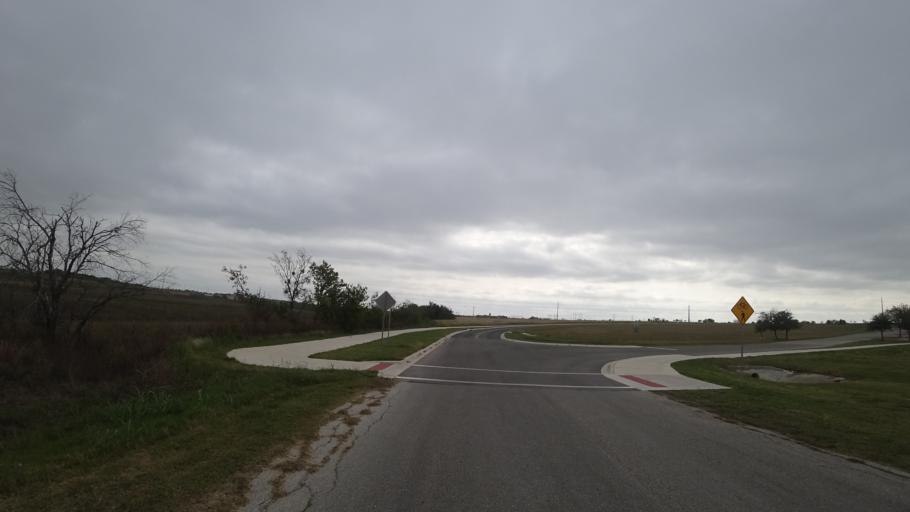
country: US
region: Texas
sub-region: Travis County
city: Pflugerville
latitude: 30.4140
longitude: -97.5917
